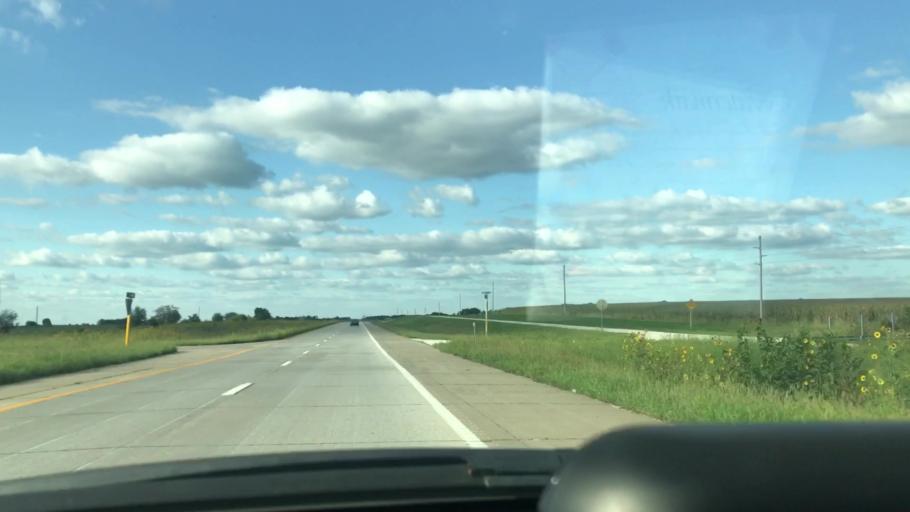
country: US
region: Missouri
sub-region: Benton County
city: Cole Camp
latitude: 38.5054
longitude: -93.2729
